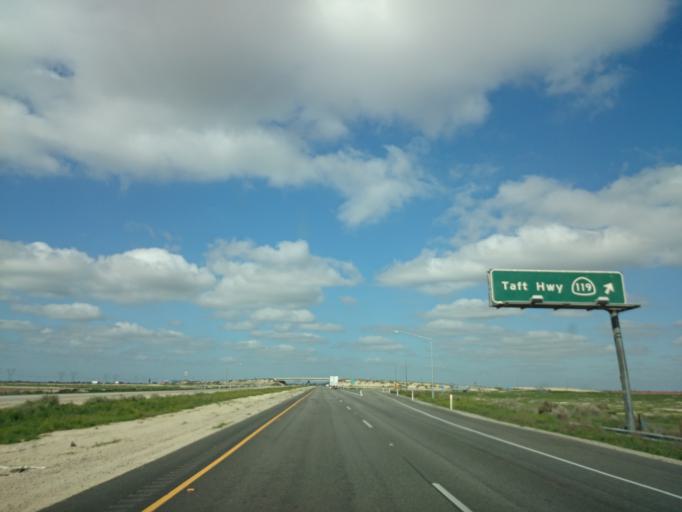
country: US
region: California
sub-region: Kern County
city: Rosedale
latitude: 35.2632
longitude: -119.2202
